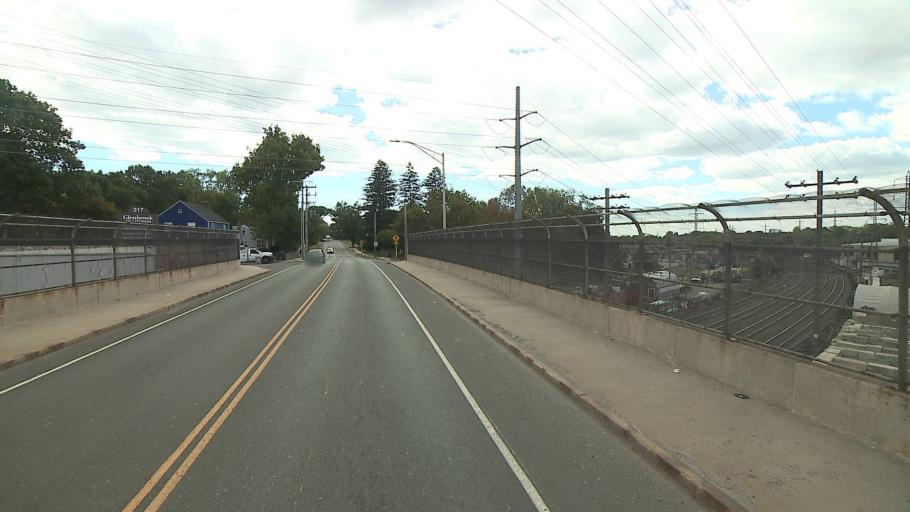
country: US
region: Connecticut
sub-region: Fairfield County
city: Stamford
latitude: 41.0695
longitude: -73.5162
